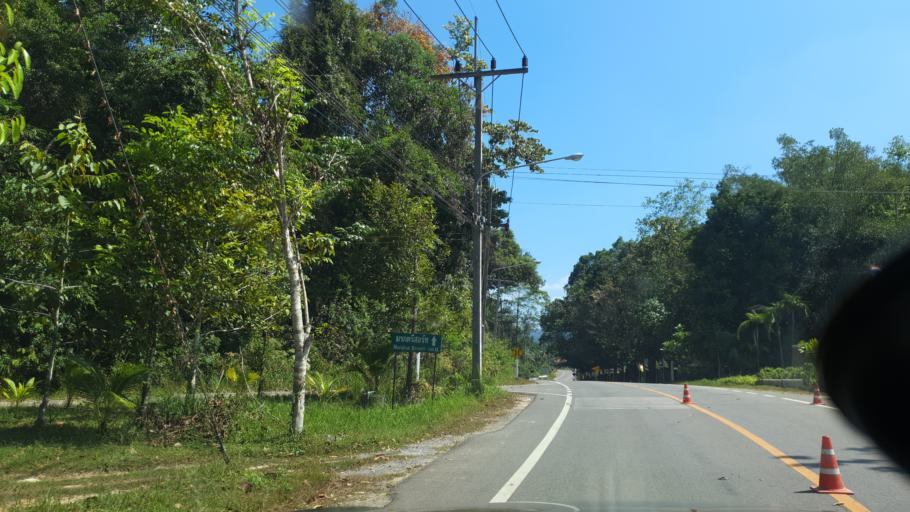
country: TH
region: Krabi
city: Khlong Thom
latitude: 7.9210
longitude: 99.2507
